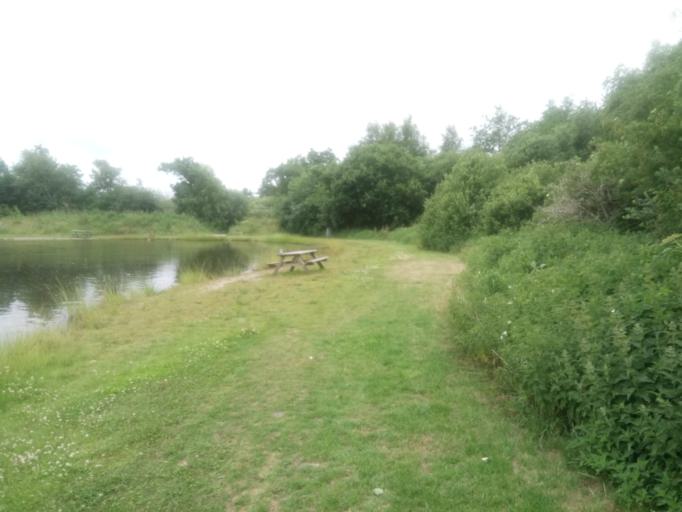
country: DK
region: Central Jutland
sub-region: Herning Kommune
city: Kibaek
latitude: 55.9552
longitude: 8.7256
